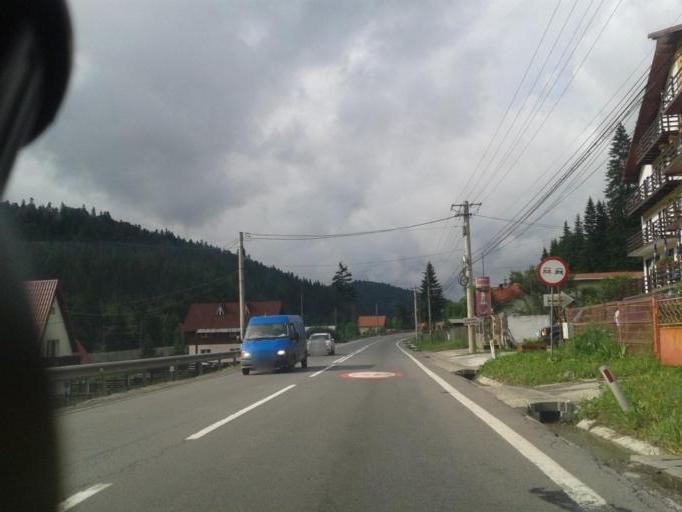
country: RO
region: Prahova
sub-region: Oras Azuga
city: Azuga
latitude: 45.4727
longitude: 25.5623
